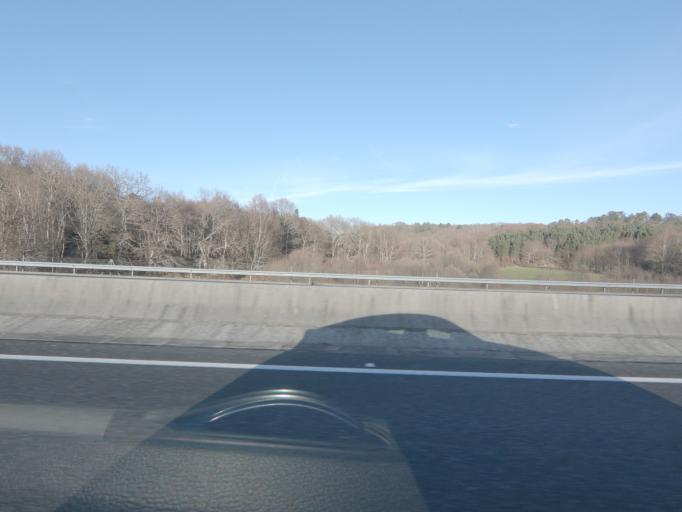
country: ES
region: Galicia
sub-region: Provincia de Pontevedra
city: Lalin
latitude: 42.6351
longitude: -8.1299
